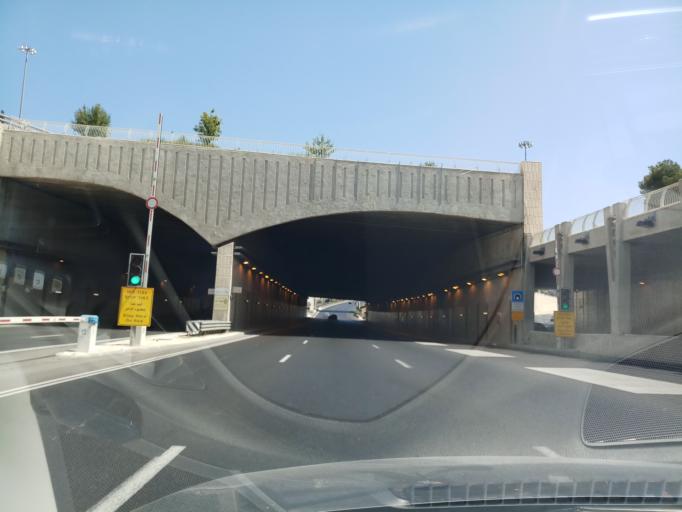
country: IL
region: Jerusalem
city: Jerusalem
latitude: 31.7551
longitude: 35.1915
